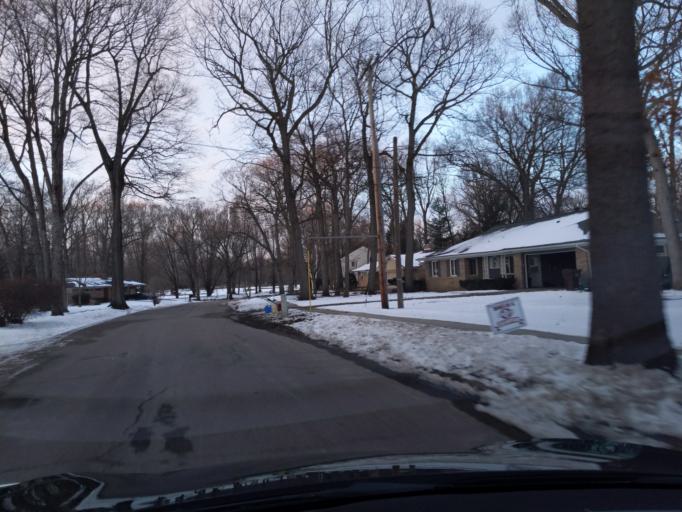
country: US
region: Michigan
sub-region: Ingham County
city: Okemos
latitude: 42.7197
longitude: -84.4375
